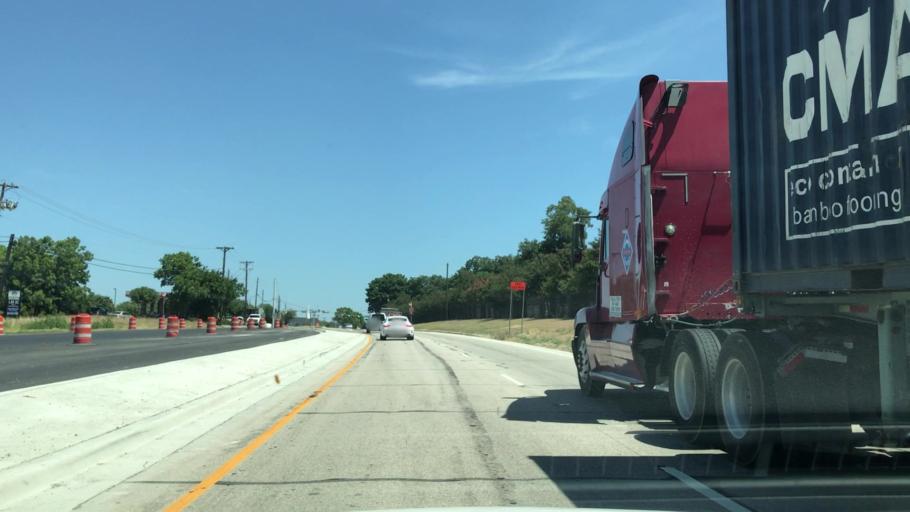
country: US
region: Texas
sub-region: Collin County
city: McKinney
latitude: 33.1771
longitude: -96.6195
